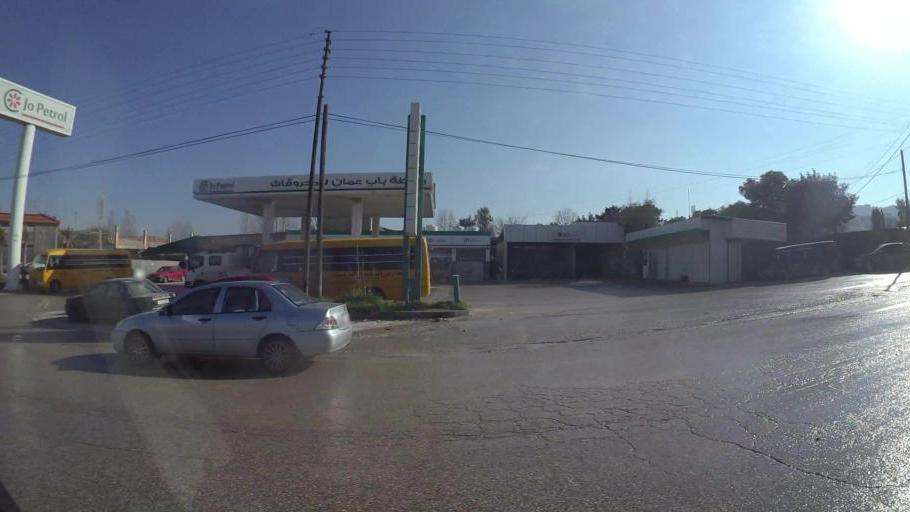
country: JO
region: Amman
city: Al Jubayhah
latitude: 32.0598
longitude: 35.8419
